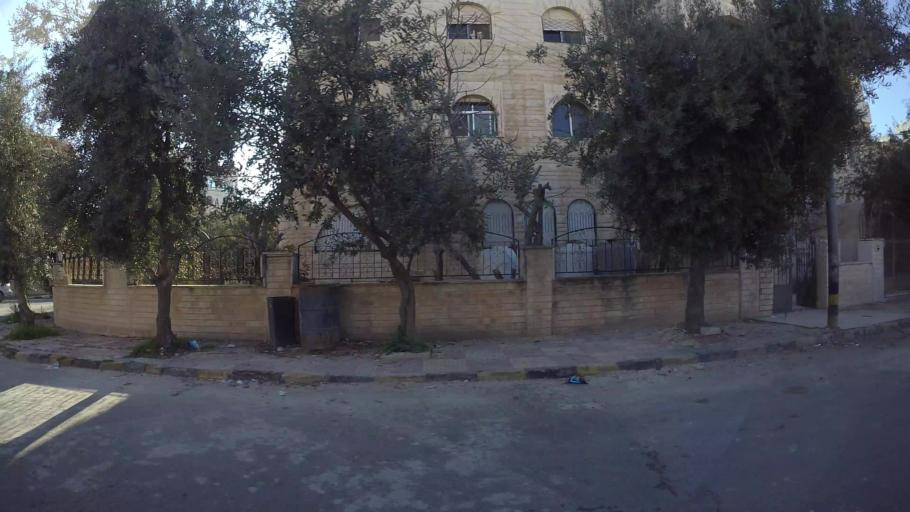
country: JO
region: Amman
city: Al Bunayyat ash Shamaliyah
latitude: 31.9002
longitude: 35.9187
